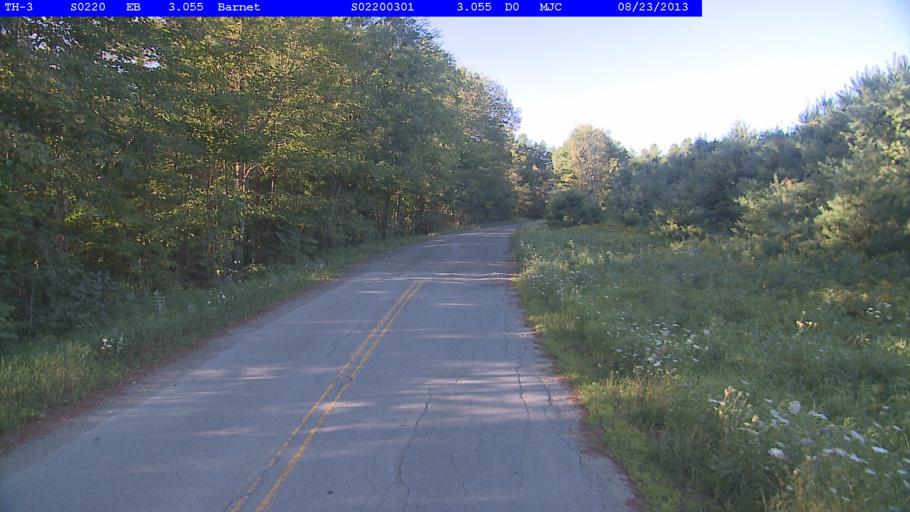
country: US
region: Vermont
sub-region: Caledonia County
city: Saint Johnsbury
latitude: 44.3380
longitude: -71.9974
